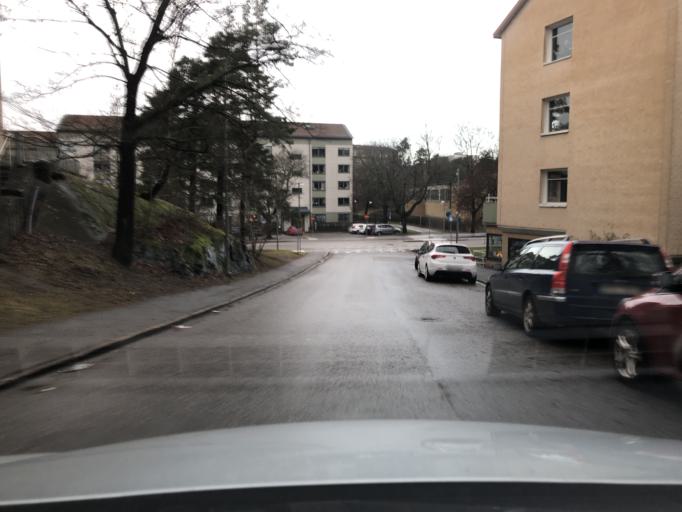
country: SE
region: Stockholm
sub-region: Stockholms Kommun
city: Arsta
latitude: 59.2976
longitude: 18.0547
